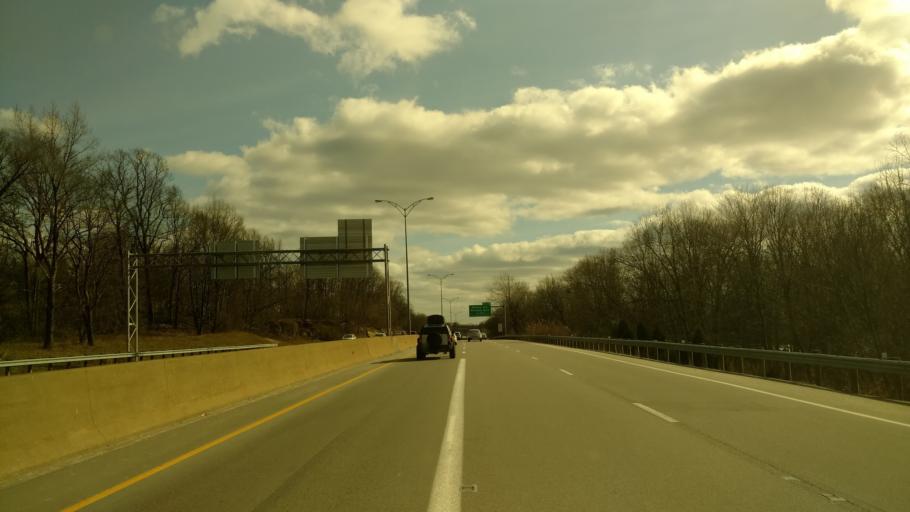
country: US
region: Ohio
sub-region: Summit County
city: Akron
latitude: 41.0570
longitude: -81.5673
